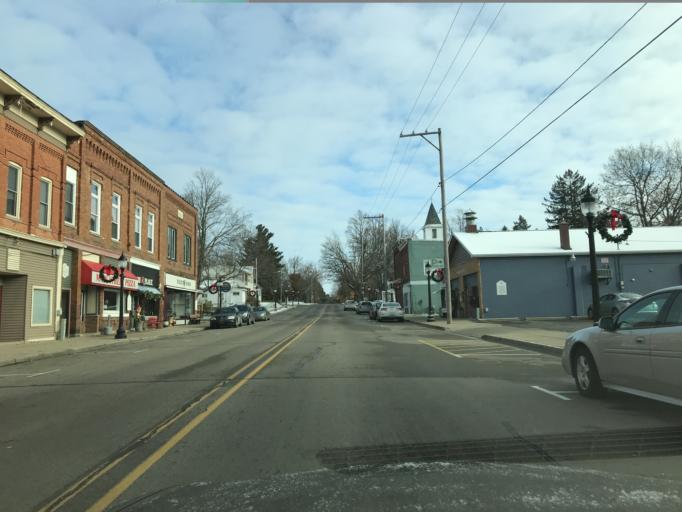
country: US
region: Michigan
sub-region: Eaton County
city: Dimondale
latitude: 42.6460
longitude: -84.6486
